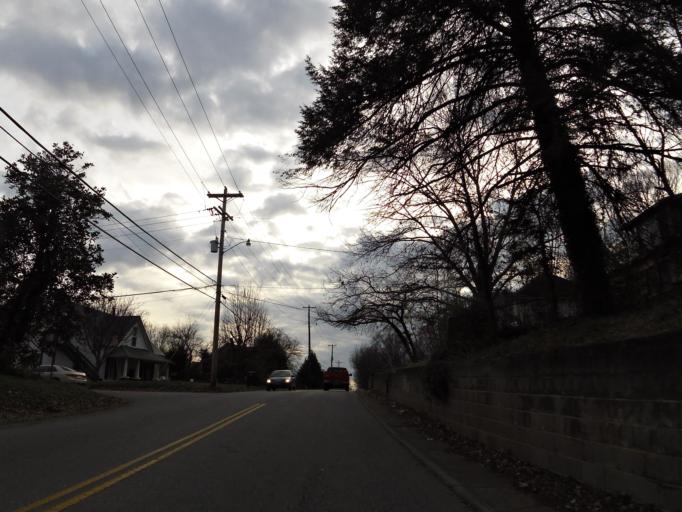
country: US
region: Tennessee
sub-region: Blount County
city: Maryville
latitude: 35.7671
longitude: -83.9615
